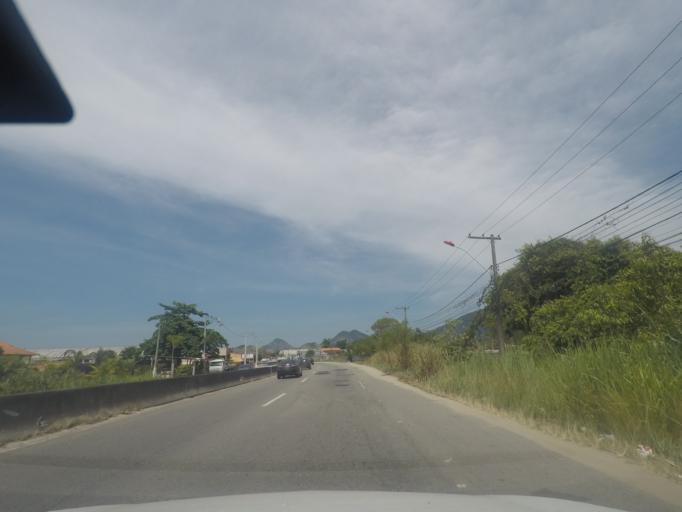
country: BR
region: Rio de Janeiro
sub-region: Marica
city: Marica
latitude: -22.9086
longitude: -42.8365
